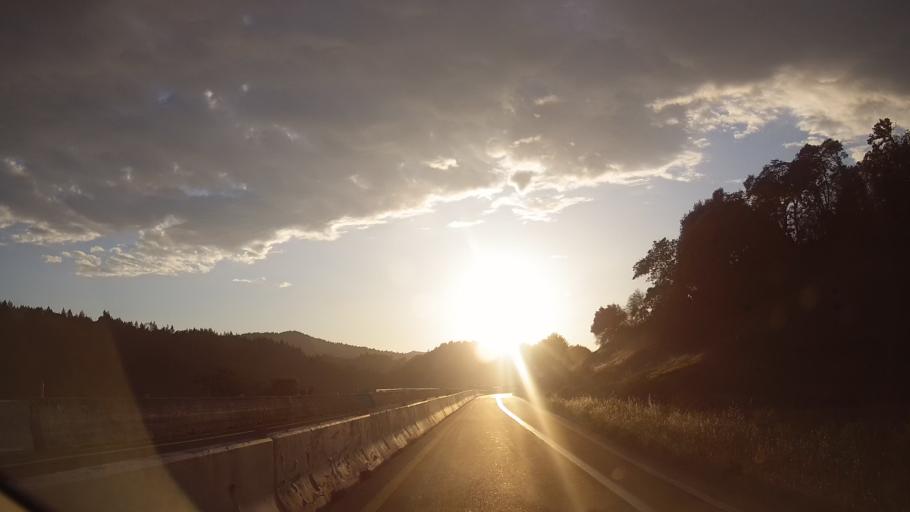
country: US
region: California
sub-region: Mendocino County
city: Redwood Valley
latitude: 39.3018
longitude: -123.2925
